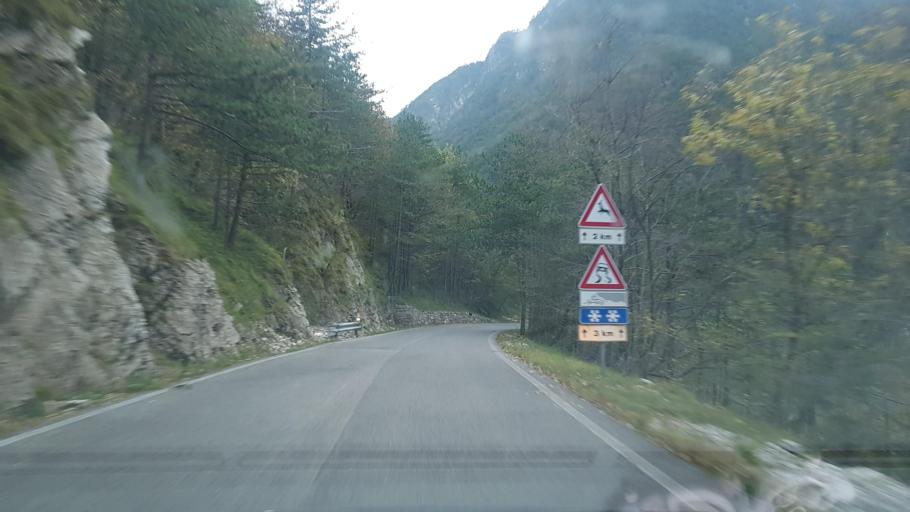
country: IT
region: Friuli Venezia Giulia
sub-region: Provincia di Udine
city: Chiaulis
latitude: 46.3332
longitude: 12.9394
